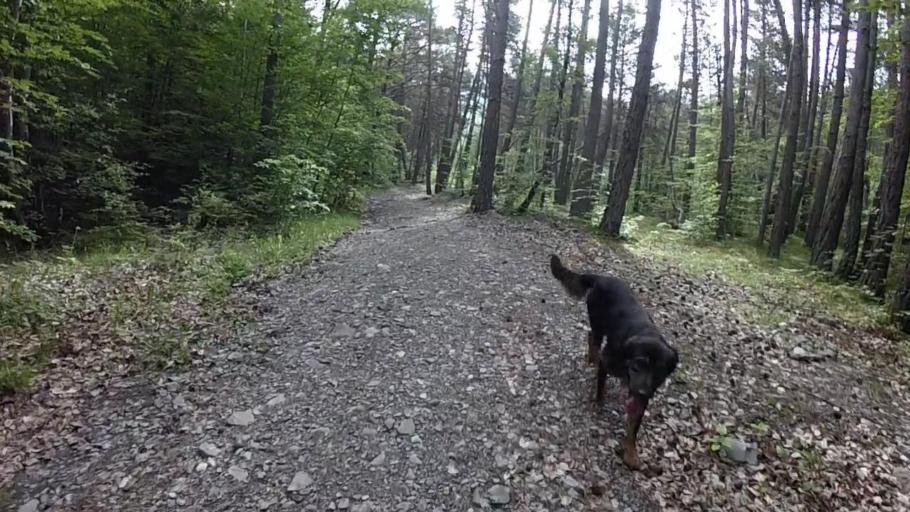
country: FR
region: Provence-Alpes-Cote d'Azur
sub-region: Departement des Alpes-de-Haute-Provence
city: Seyne-les-Alpes
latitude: 44.4094
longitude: 6.3432
